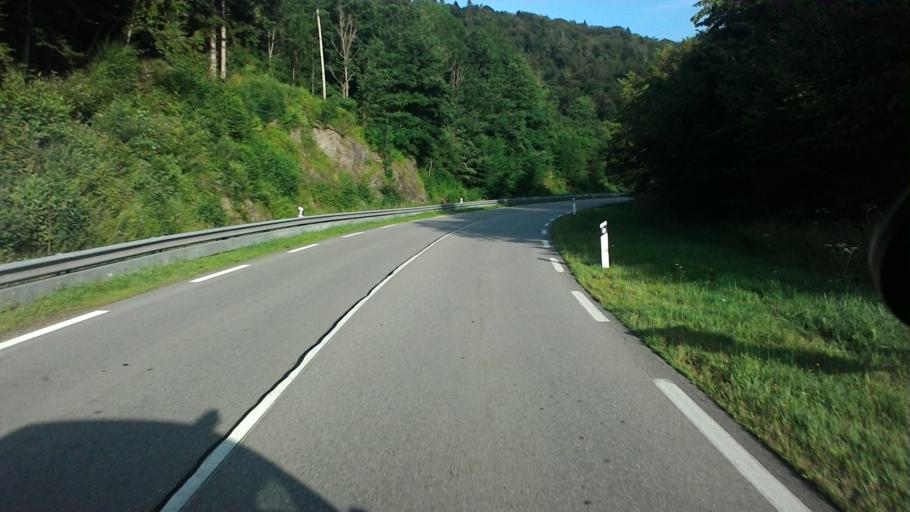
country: FR
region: Lorraine
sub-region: Departement des Vosges
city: Saint-Maurice-sur-Moselle
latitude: 47.8646
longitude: 6.8082
